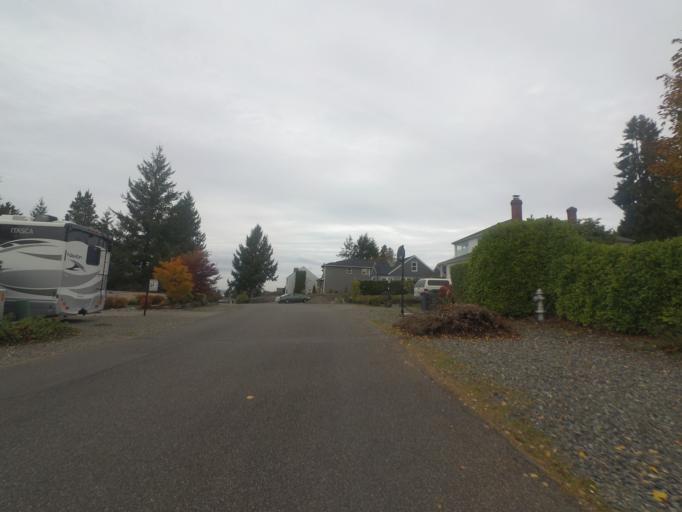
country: US
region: Washington
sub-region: Pierce County
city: University Place
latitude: 47.2199
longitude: -122.5658
